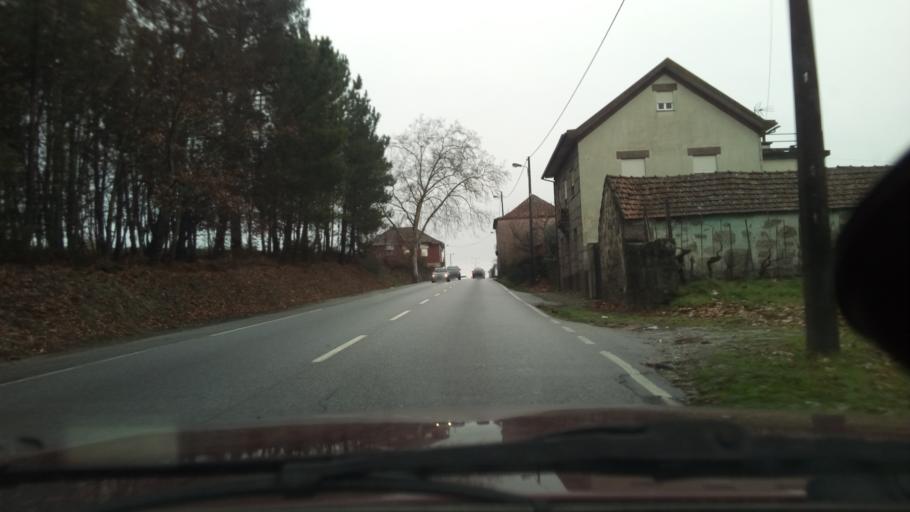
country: PT
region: Viseu
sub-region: Viseu
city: Rio de Loba
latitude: 40.6498
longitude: -7.8777
